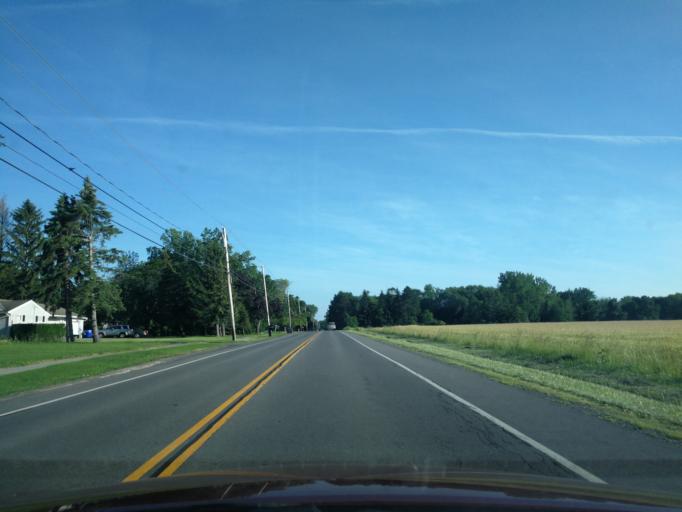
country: US
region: New York
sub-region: Monroe County
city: Greece
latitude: 43.2589
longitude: -77.7154
